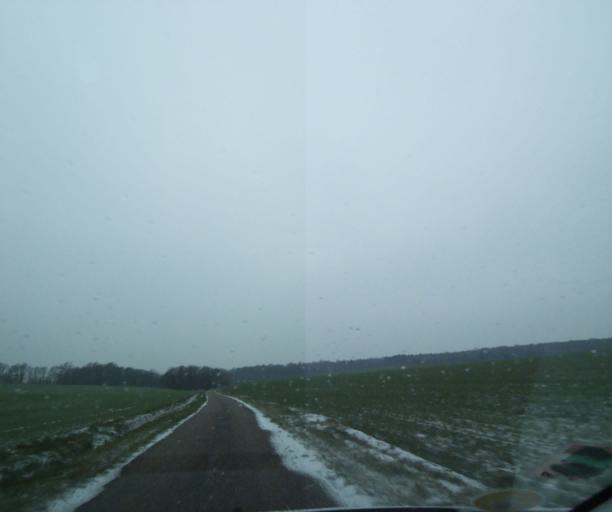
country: FR
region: Champagne-Ardenne
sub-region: Departement de la Haute-Marne
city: Wassy
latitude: 48.4632
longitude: 5.0218
